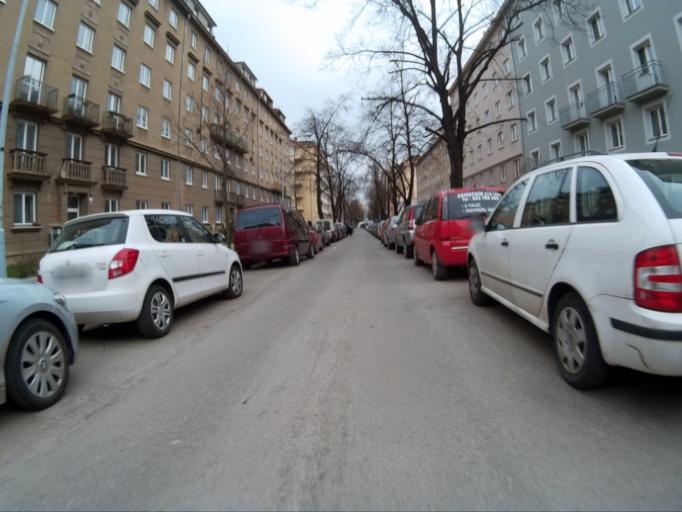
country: CZ
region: South Moravian
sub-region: Mesto Brno
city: Brno
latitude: 49.2087
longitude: 16.6008
